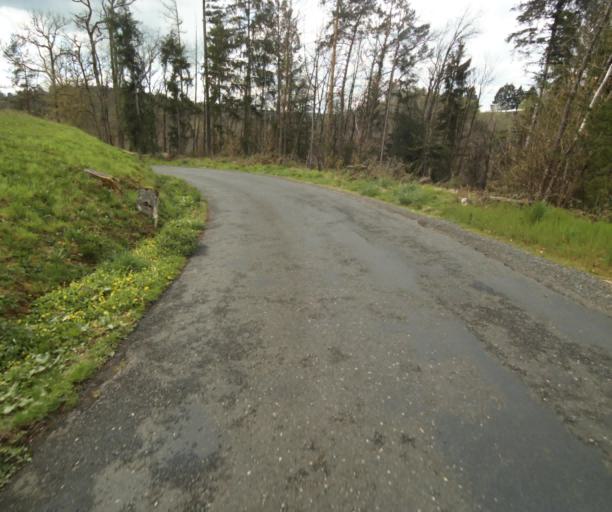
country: FR
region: Limousin
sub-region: Departement de la Correze
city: Tulle
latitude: 45.2811
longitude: 1.7373
